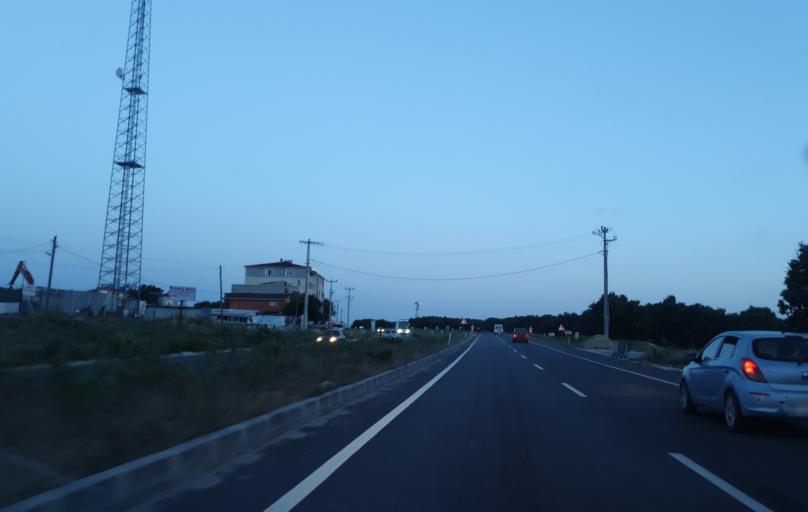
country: TR
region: Tekirdag
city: Saray
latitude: 41.3667
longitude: 27.9416
